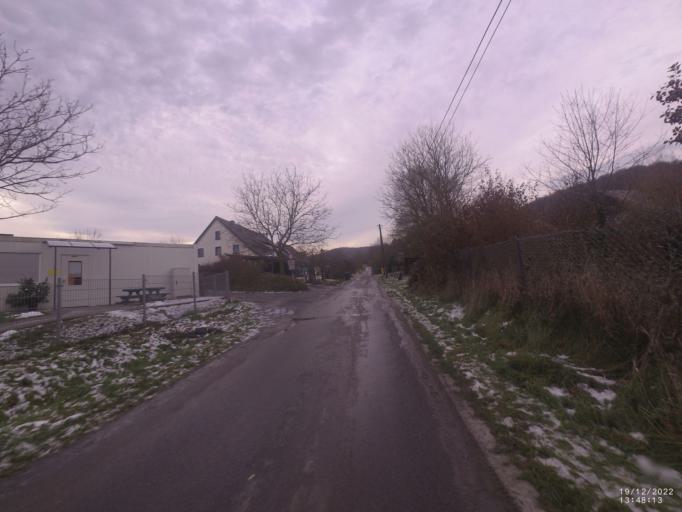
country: DE
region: Rheinland-Pfalz
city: Unkel
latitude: 50.6106
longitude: 7.1954
